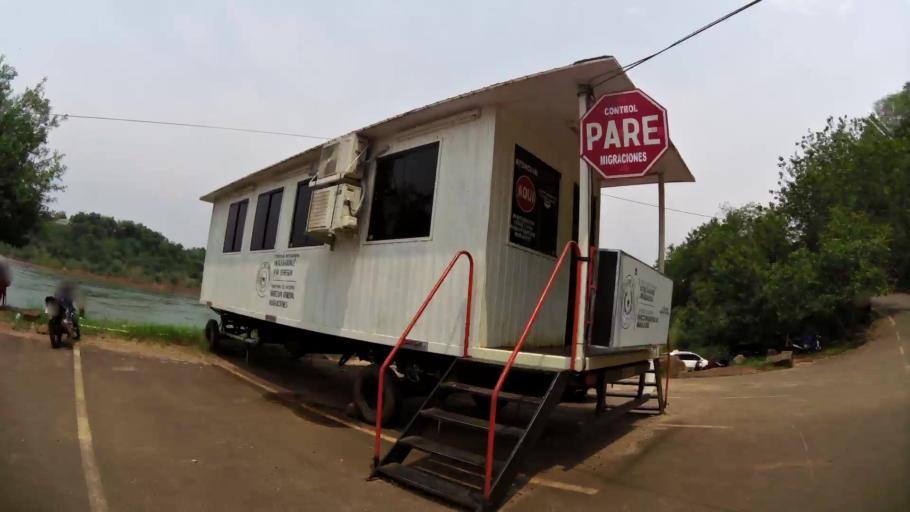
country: AR
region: Misiones
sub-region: Departamento de Iguazu
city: Puerto Iguazu
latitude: -25.5931
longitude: -54.5968
